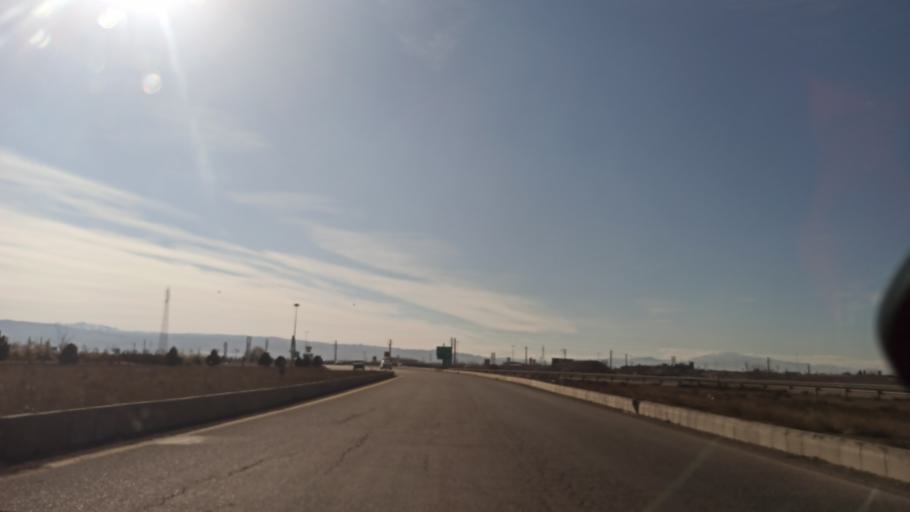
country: IR
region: Qazvin
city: Bu'in Zahra
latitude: 35.7686
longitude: 50.0845
